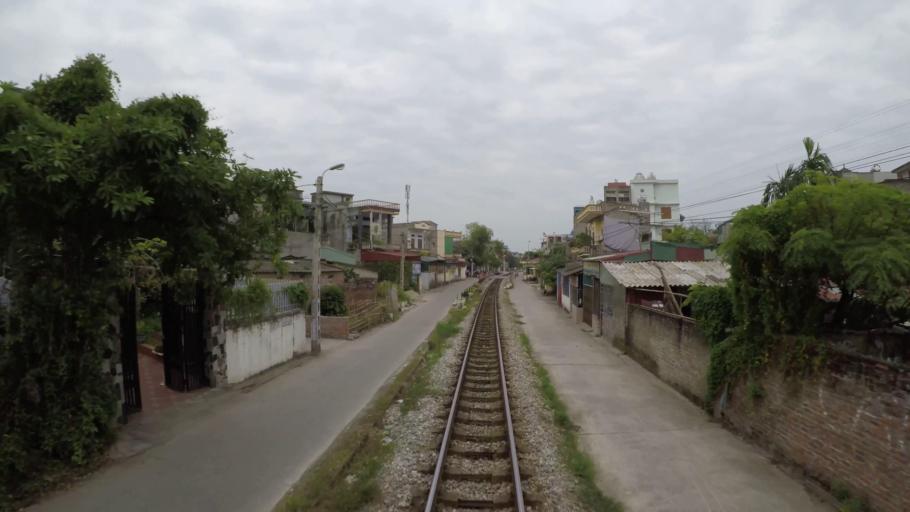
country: VN
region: Hai Duong
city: Lai Cach
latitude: 20.9433
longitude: 106.2880
